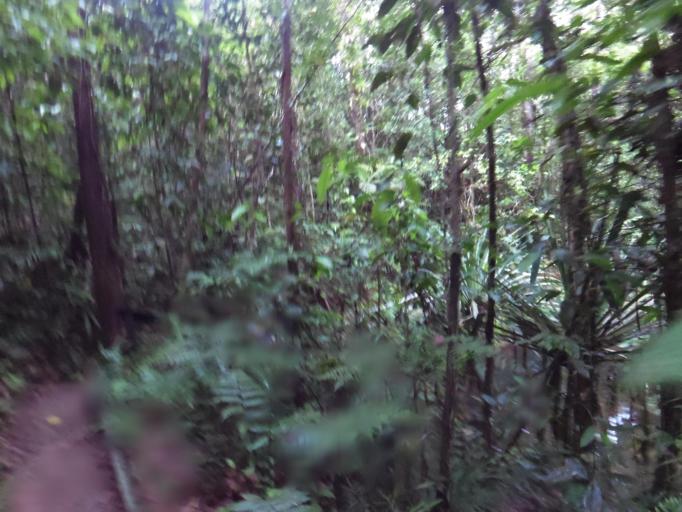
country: FJ
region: Central
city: Suva
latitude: -18.0598
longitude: 178.4704
